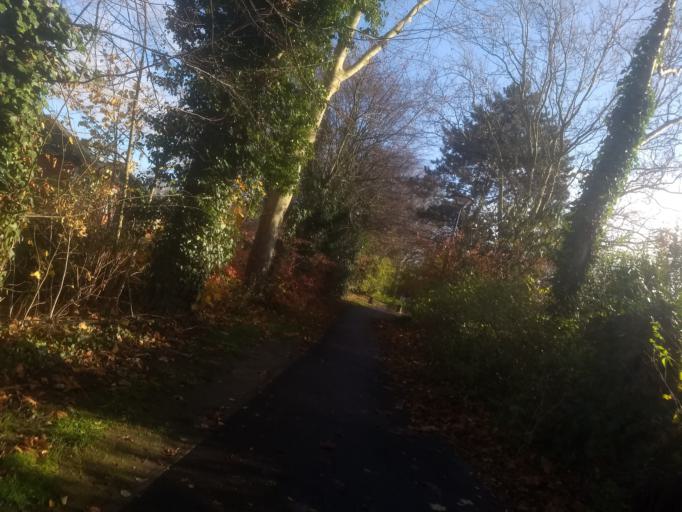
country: FR
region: Nord-Pas-de-Calais
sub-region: Departement du Pas-de-Calais
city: Anzin-Saint-Aubin
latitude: 50.2985
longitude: 2.7479
